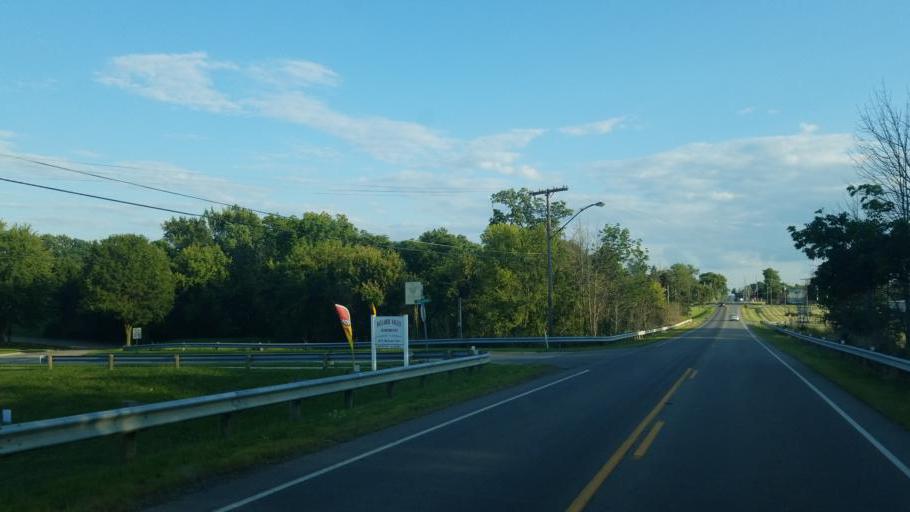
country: US
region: Ohio
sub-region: Huron County
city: Willard
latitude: 41.0569
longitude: -82.7163
